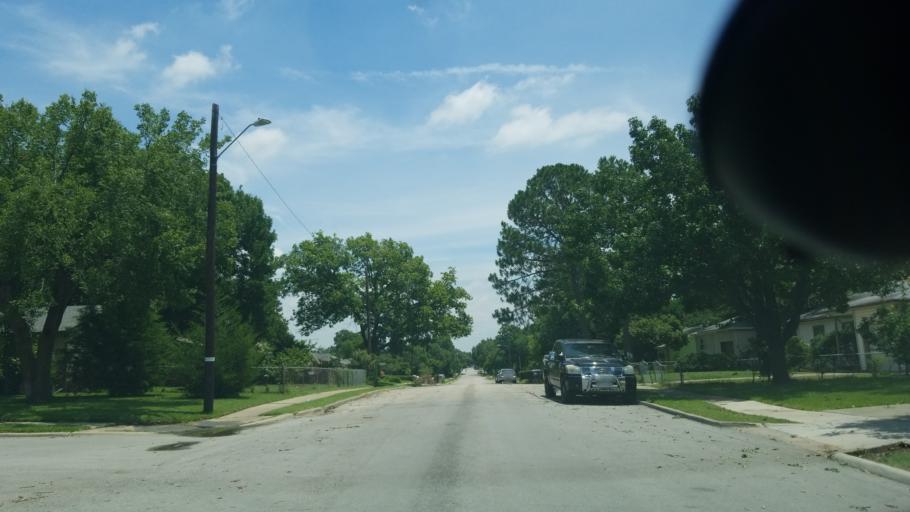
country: US
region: Texas
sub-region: Dallas County
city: Irving
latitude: 32.8464
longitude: -96.9744
